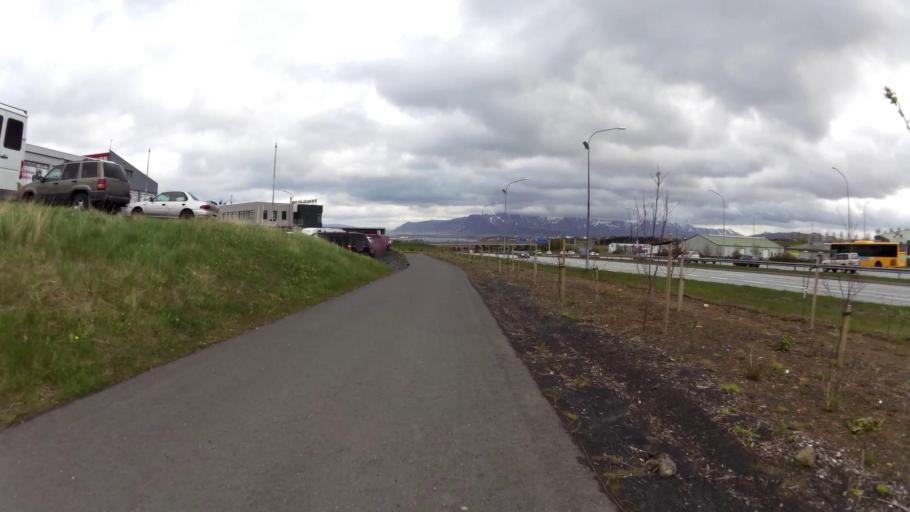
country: IS
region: Capital Region
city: Reykjavik
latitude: 64.1114
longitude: -21.8450
